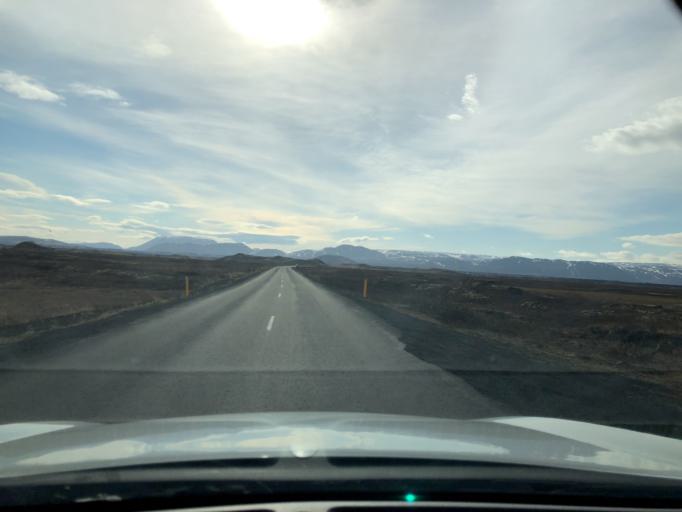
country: IS
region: Northeast
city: Laugar
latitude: 65.5637
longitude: -17.0164
